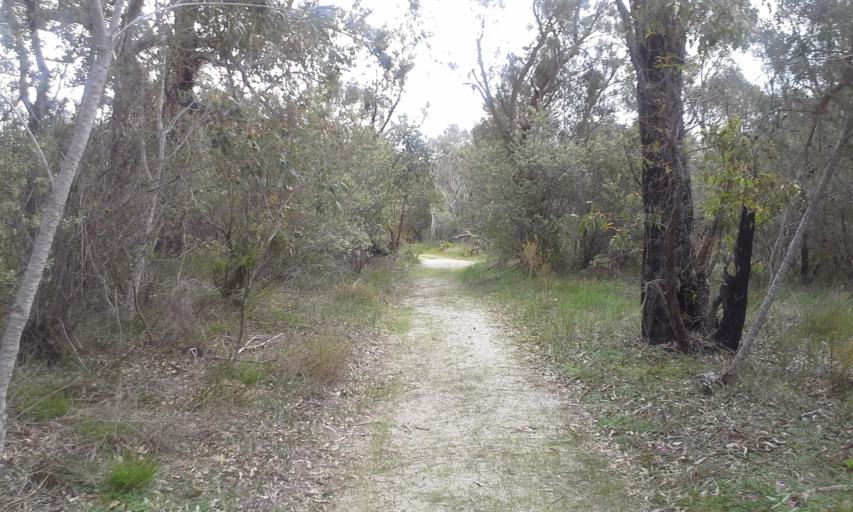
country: AU
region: Western Australia
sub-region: City of Perth
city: West Perth
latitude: -31.9587
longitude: 115.8345
